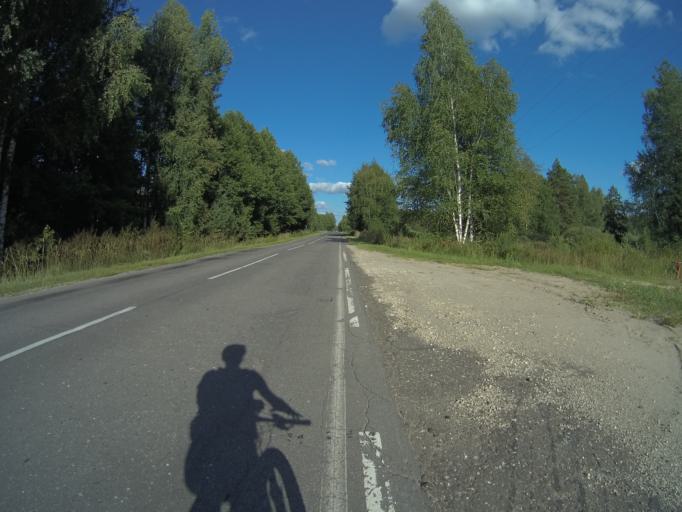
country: RU
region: Vladimir
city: Mezinovskiy
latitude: 55.5954
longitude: 40.3778
